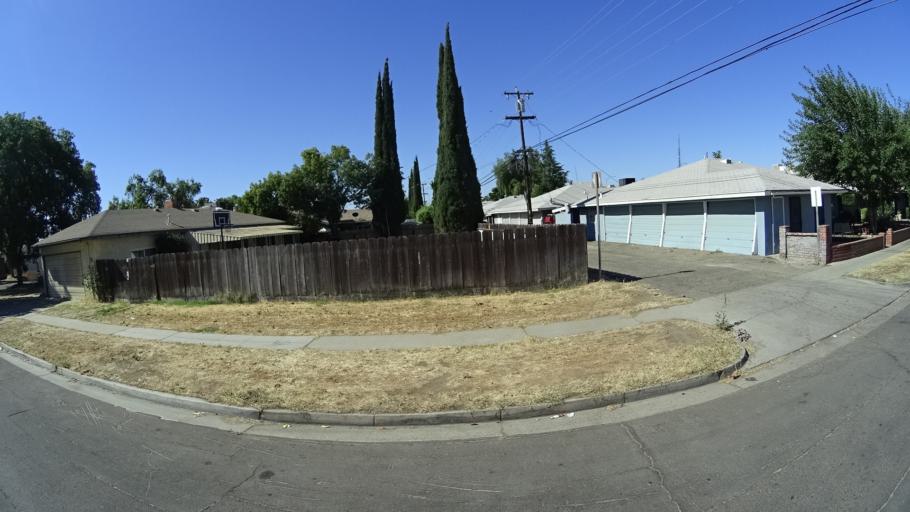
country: US
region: California
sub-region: Fresno County
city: Fresno
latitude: 36.7786
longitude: -119.7718
